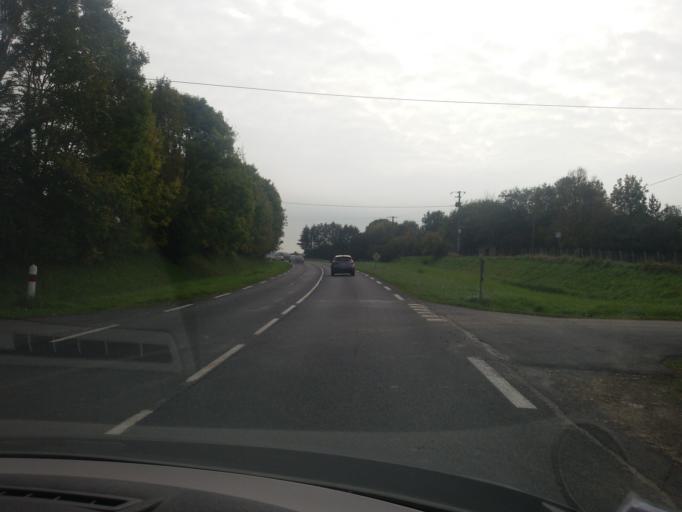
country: FR
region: Lower Normandy
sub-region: Departement du Calvados
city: Dives-sur-Mer
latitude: 49.2451
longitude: -0.1028
